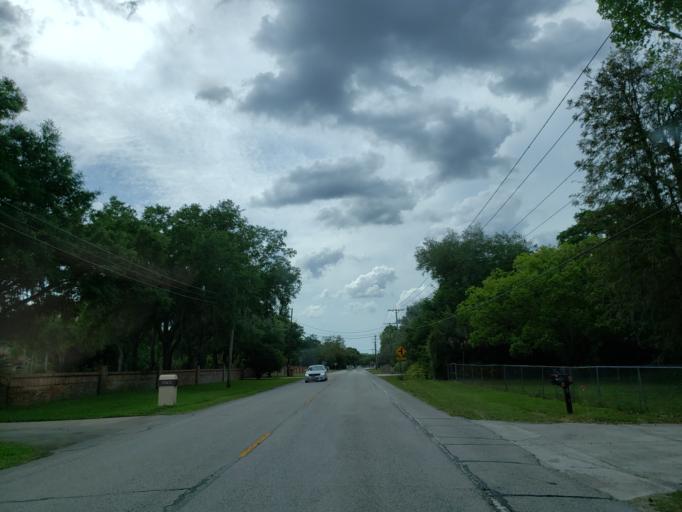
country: US
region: Florida
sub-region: Hillsborough County
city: Keystone
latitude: 28.1401
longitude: -82.6349
